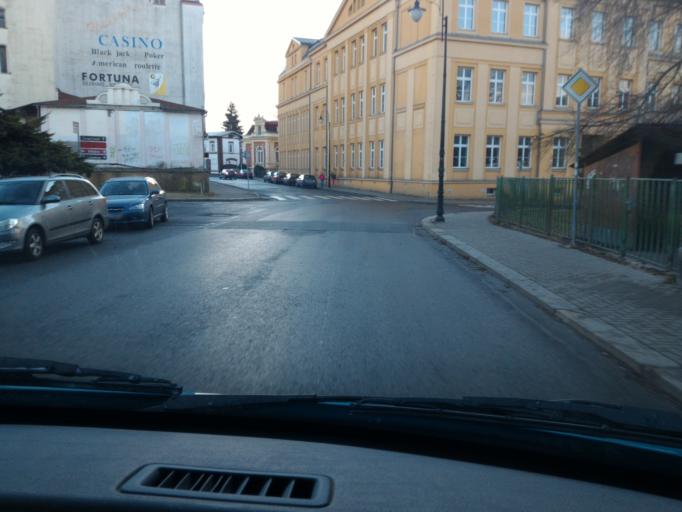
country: CZ
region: Ustecky
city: Varnsdorf
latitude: 50.9107
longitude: 14.6256
